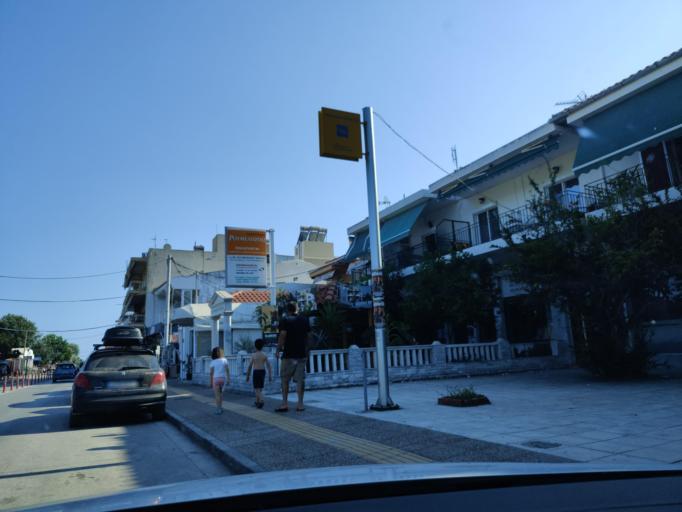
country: GR
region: East Macedonia and Thrace
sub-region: Nomos Kavalas
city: Nea Peramos
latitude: 40.8404
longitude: 24.3049
